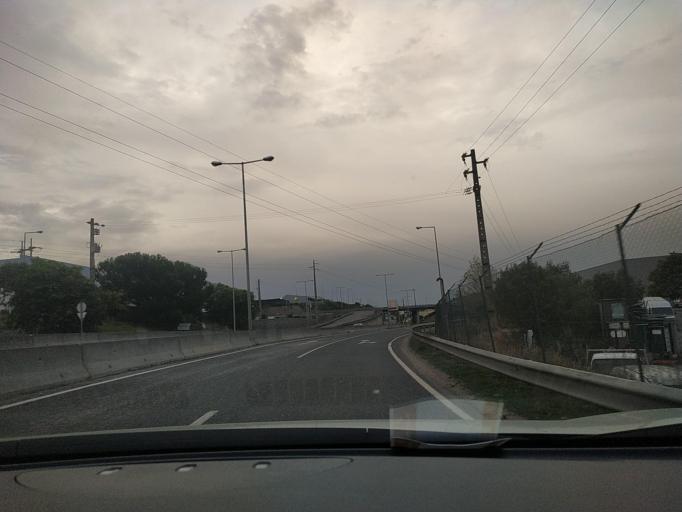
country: PT
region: Lisbon
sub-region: Loures
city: Santo Antao do Tojal
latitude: 38.8618
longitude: -9.1127
